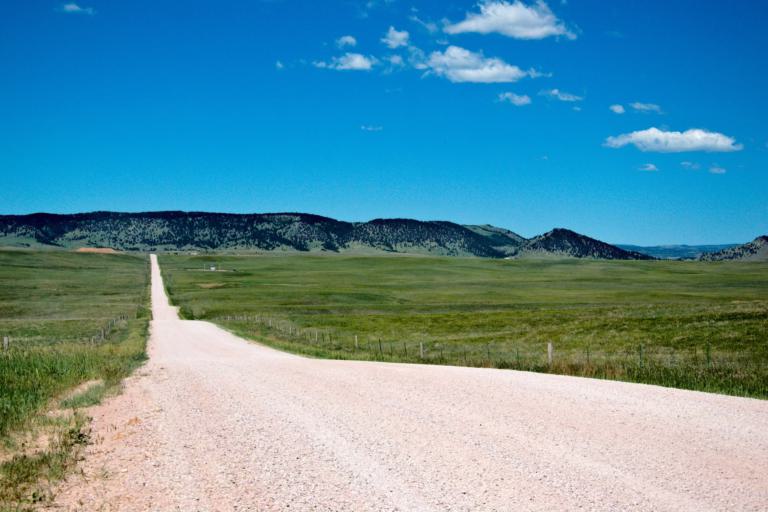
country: US
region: South Dakota
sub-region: Fall River County
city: Hot Springs
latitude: 43.4918
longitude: -103.2640
